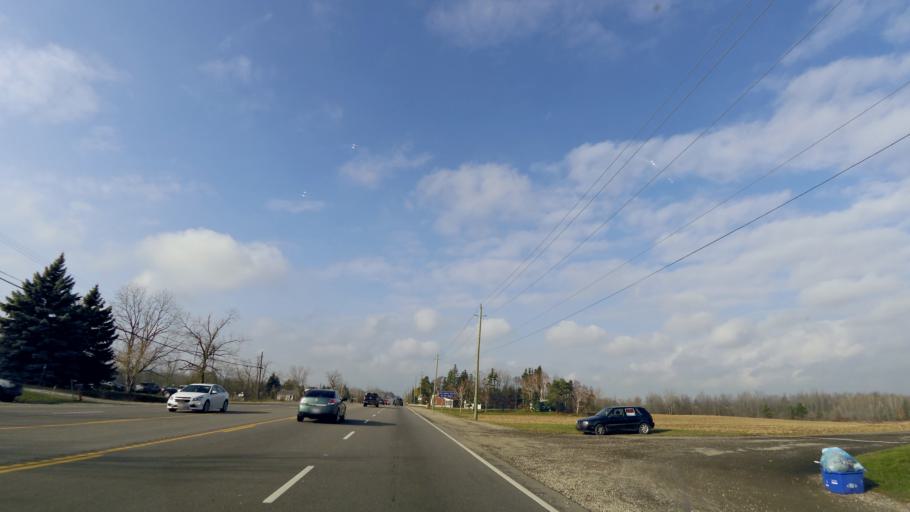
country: CA
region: Ontario
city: Hamilton
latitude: 43.3233
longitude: -79.9328
